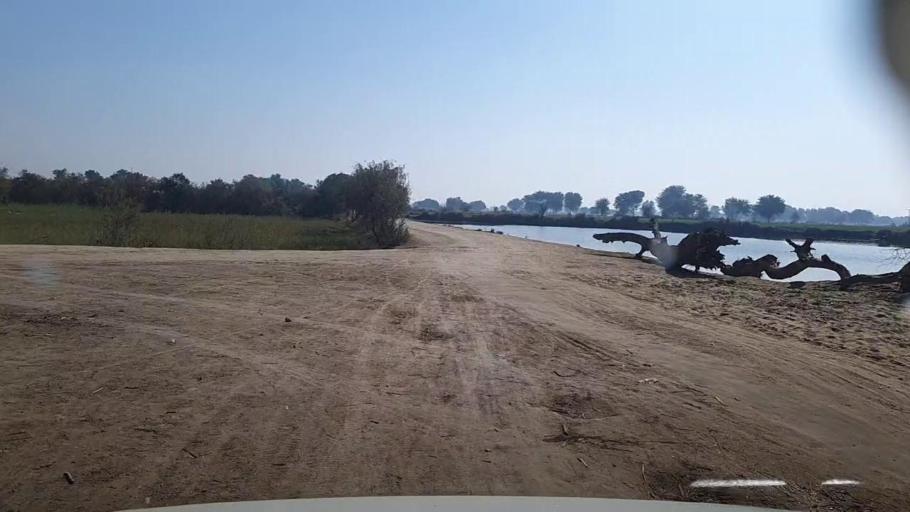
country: PK
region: Sindh
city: Khairpur
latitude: 27.9538
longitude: 69.6863
